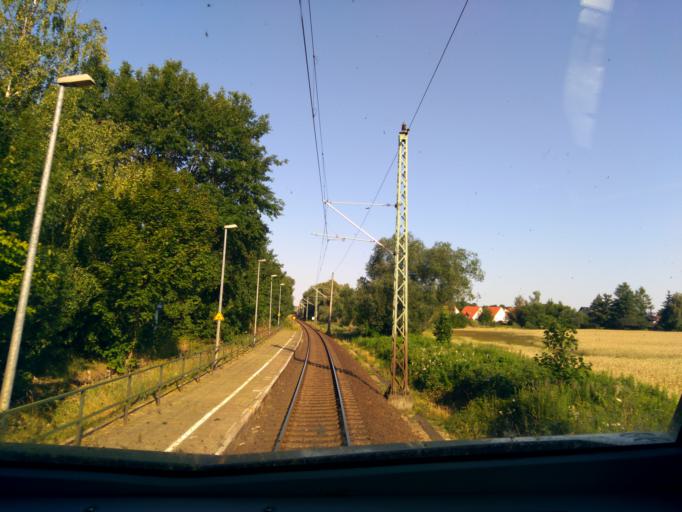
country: DE
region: Brandenburg
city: Kolkwitz
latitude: 51.7578
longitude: 14.2497
